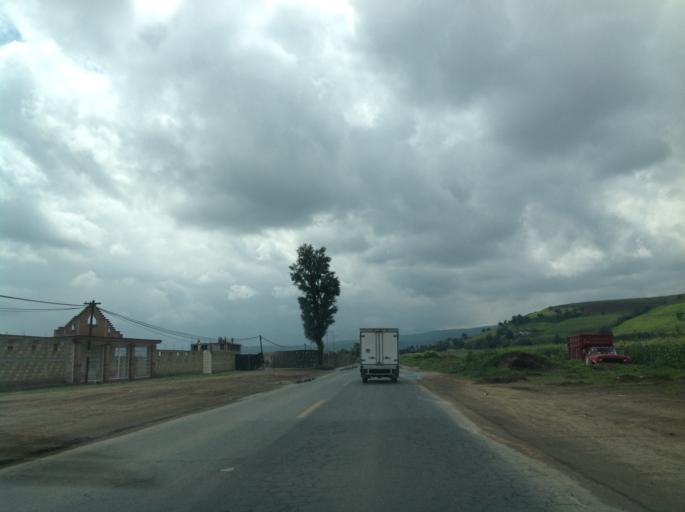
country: MX
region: Mexico
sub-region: Tenango del Valle
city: Santa Maria Jajalpa
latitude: 19.1171
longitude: -99.5503
